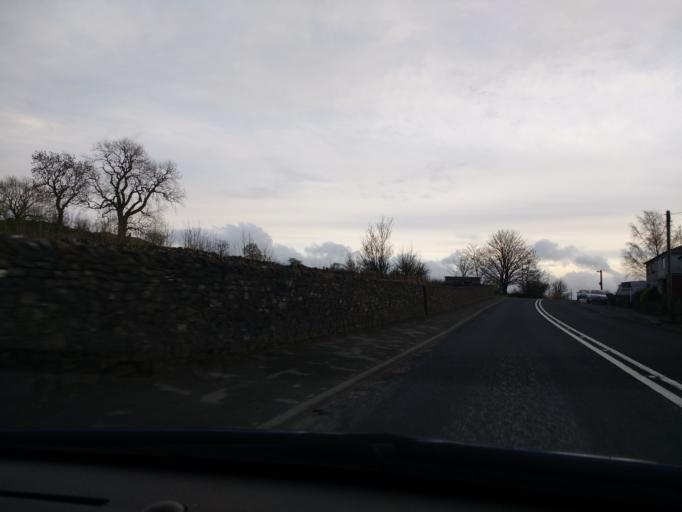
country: GB
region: England
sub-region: North Yorkshire
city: Settle
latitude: 54.0860
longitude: -2.2748
